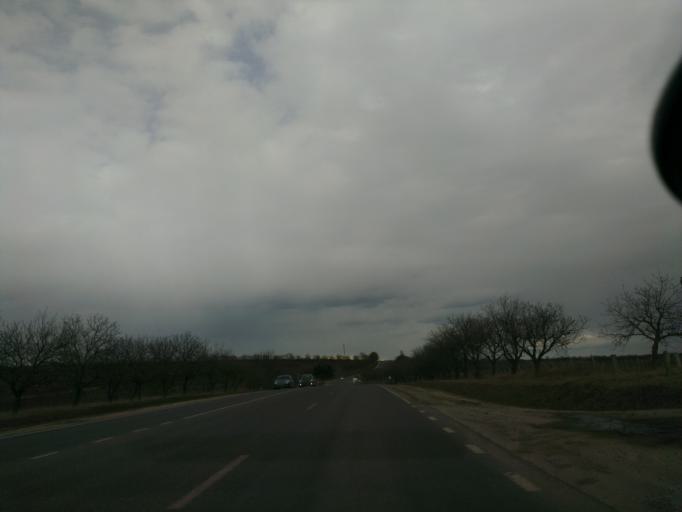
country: MD
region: Hincesti
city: Hincesti
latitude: 46.8530
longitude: 28.6230
